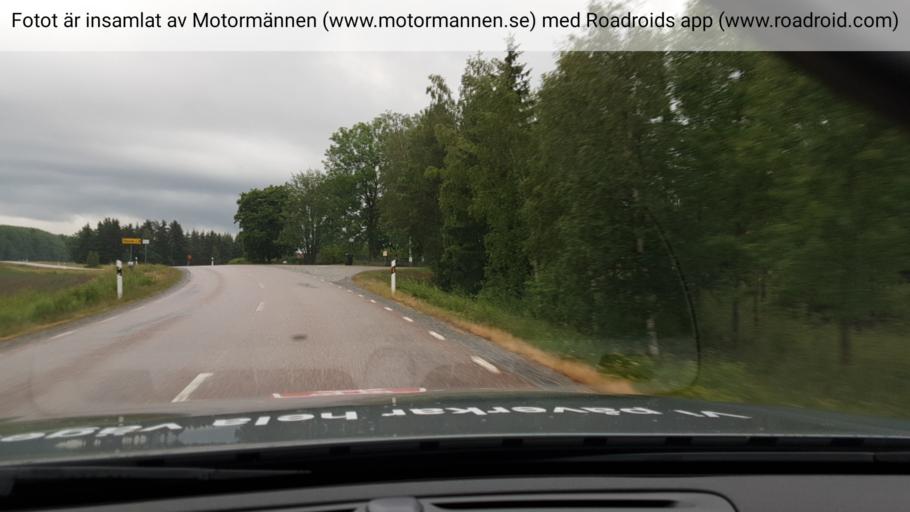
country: SE
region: Vaestmanland
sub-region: Sala Kommun
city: Sala
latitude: 59.9163
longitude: 16.4662
